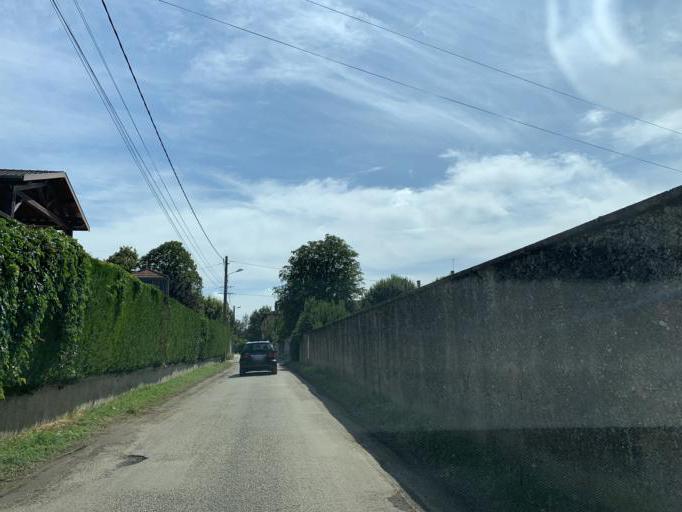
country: FR
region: Rhone-Alpes
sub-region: Departement de l'Ain
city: Thil
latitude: 45.8135
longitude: 5.0205
